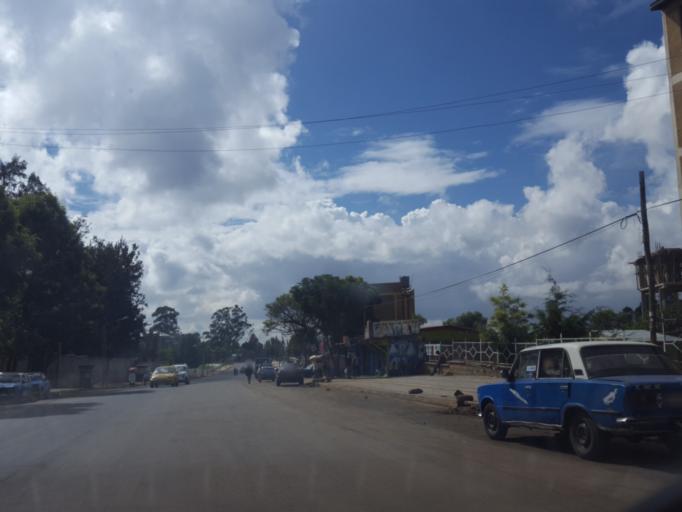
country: ET
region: Adis Abeba
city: Addis Ababa
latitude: 9.0604
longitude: 38.7620
